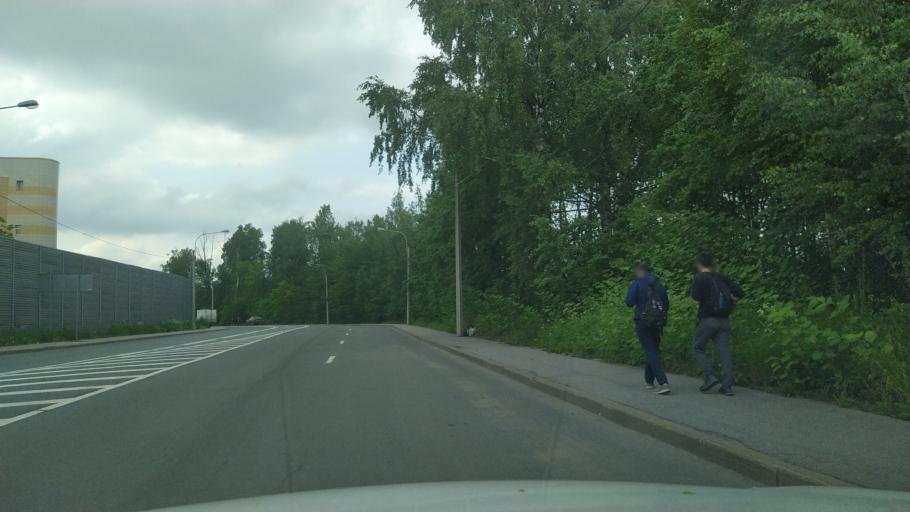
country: RU
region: St.-Petersburg
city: Krasnogvargeisky
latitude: 59.9841
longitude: 30.4407
